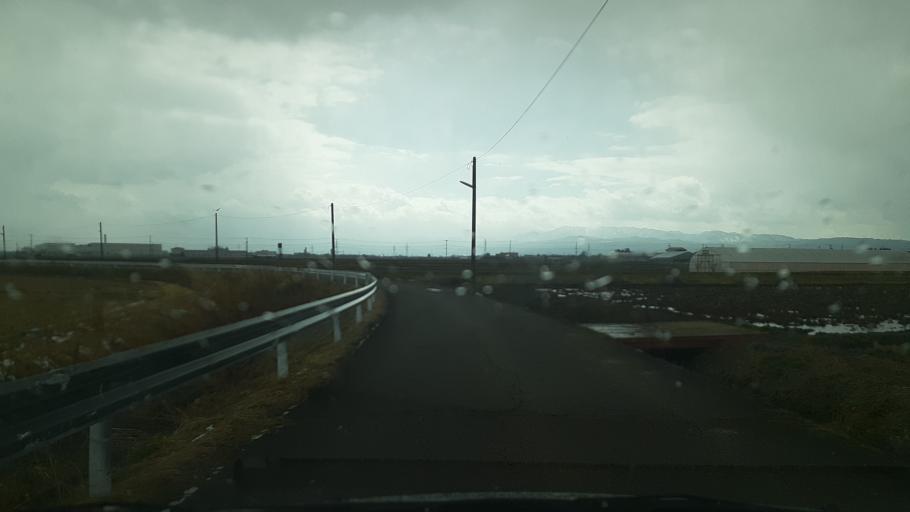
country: JP
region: Fukushima
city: Kitakata
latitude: 37.5569
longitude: 139.8816
